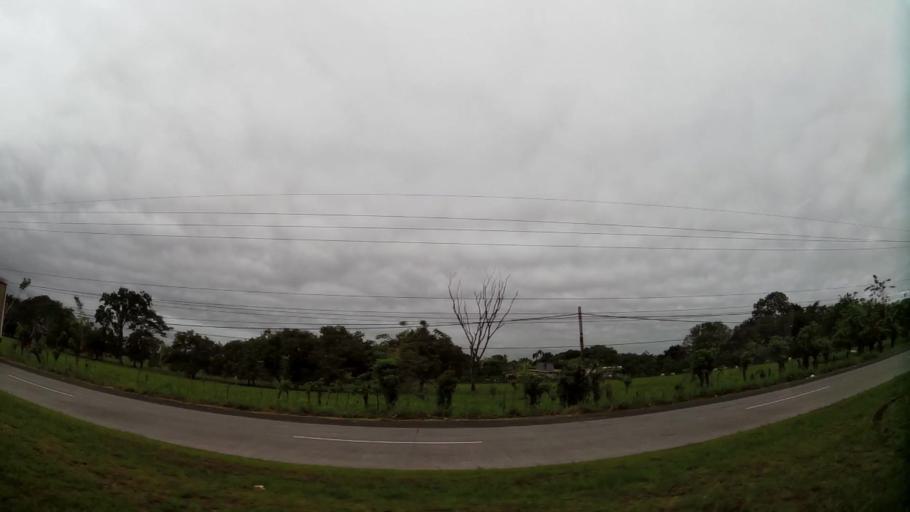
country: PA
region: Chiriqui
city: Tijera
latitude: 8.4808
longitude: -82.5573
